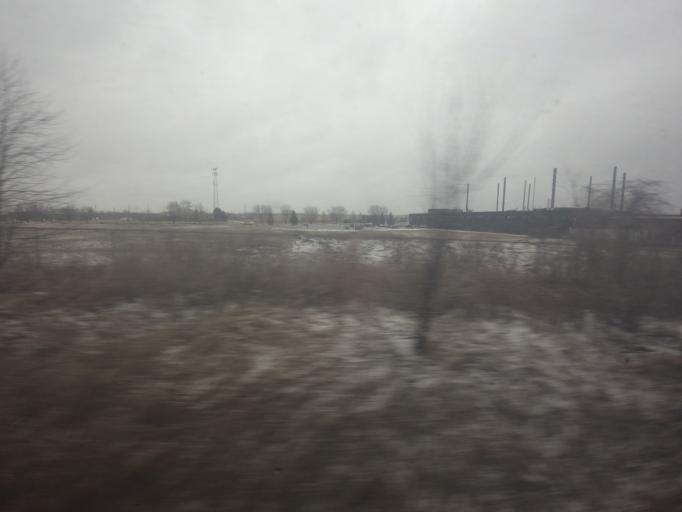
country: CA
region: Ontario
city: Brockville
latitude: 44.6137
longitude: -75.6973
